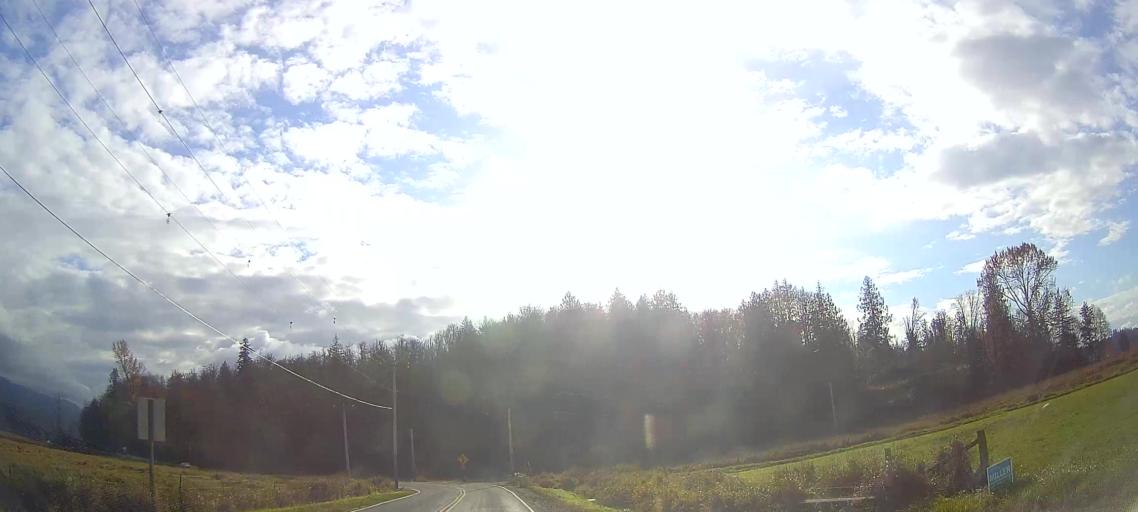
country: US
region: Washington
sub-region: Skagit County
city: Clear Lake
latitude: 48.4501
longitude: -122.2255
